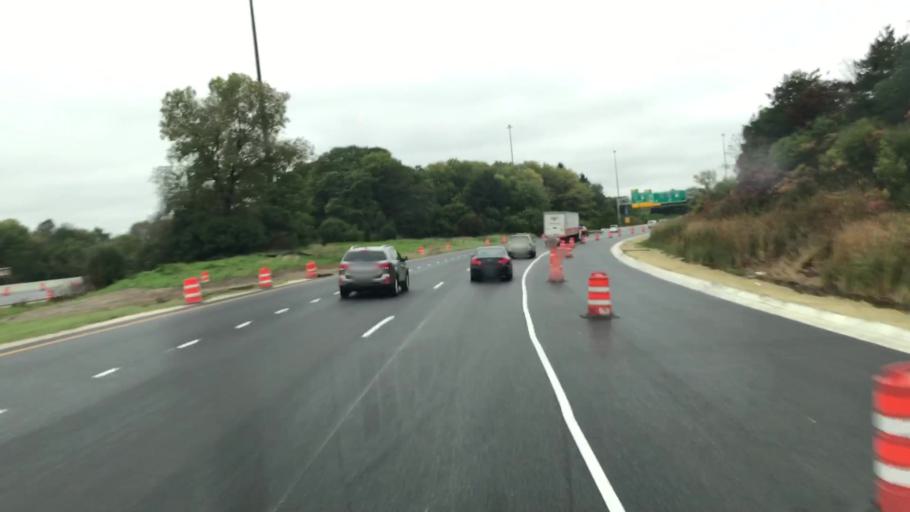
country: US
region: Wisconsin
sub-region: Milwaukee County
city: Greenfield
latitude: 42.9618
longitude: -88.0308
